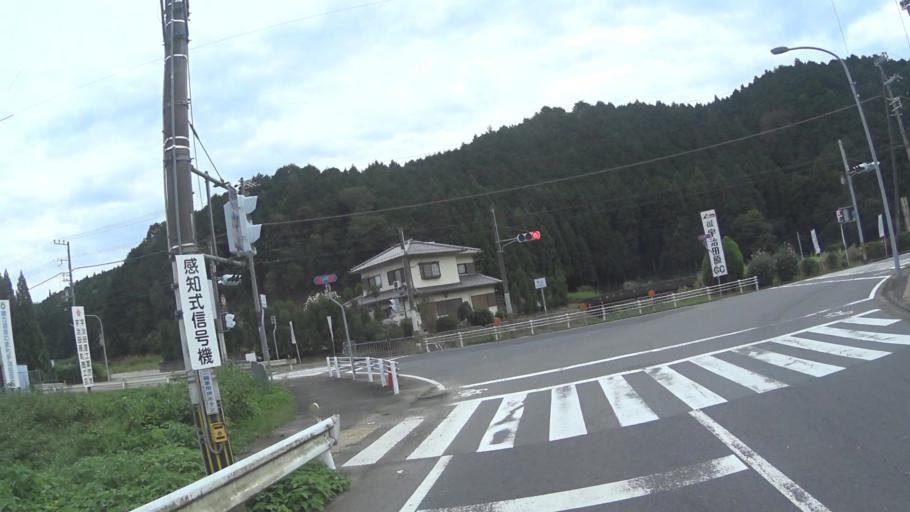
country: JP
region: Kyoto
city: Uji
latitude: 34.8598
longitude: 135.8730
